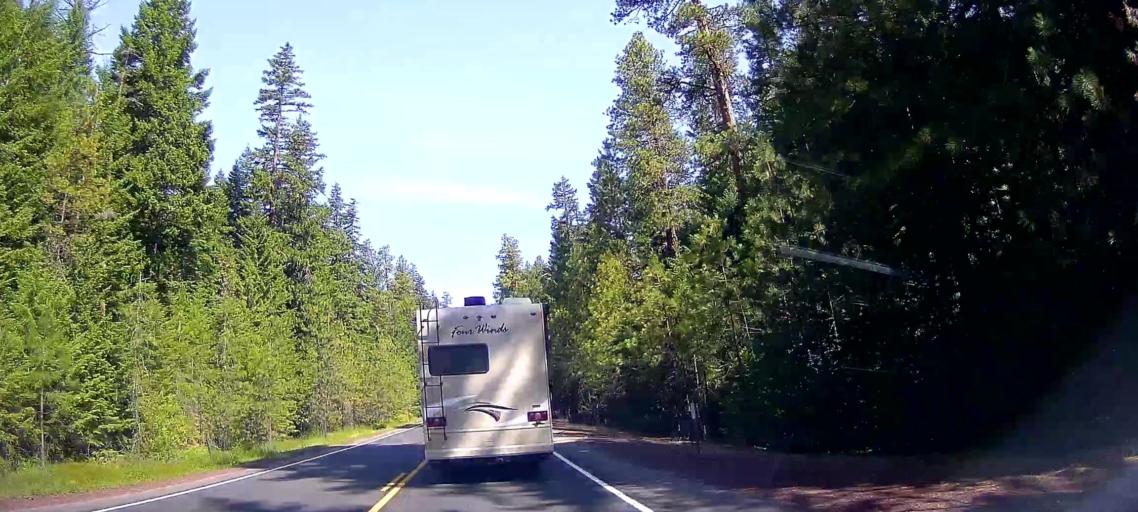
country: US
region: Oregon
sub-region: Jefferson County
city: Warm Springs
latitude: 45.0760
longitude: -121.5370
